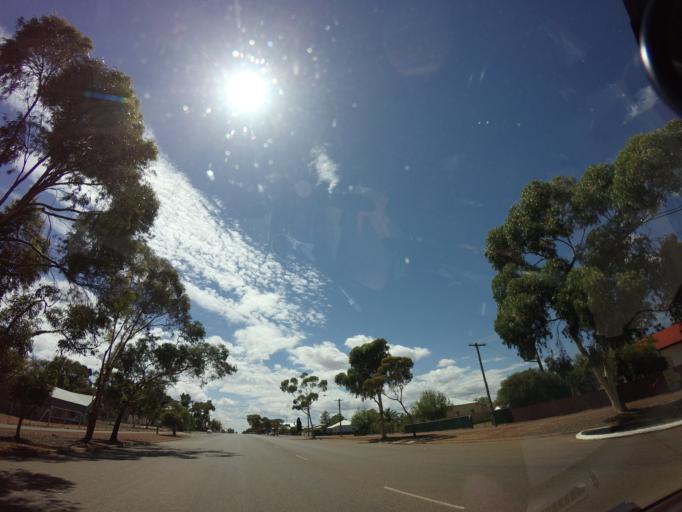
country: AU
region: Western Australia
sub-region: Kalgoorlie/Boulder
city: Boulder
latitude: -30.9546
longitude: 121.1601
